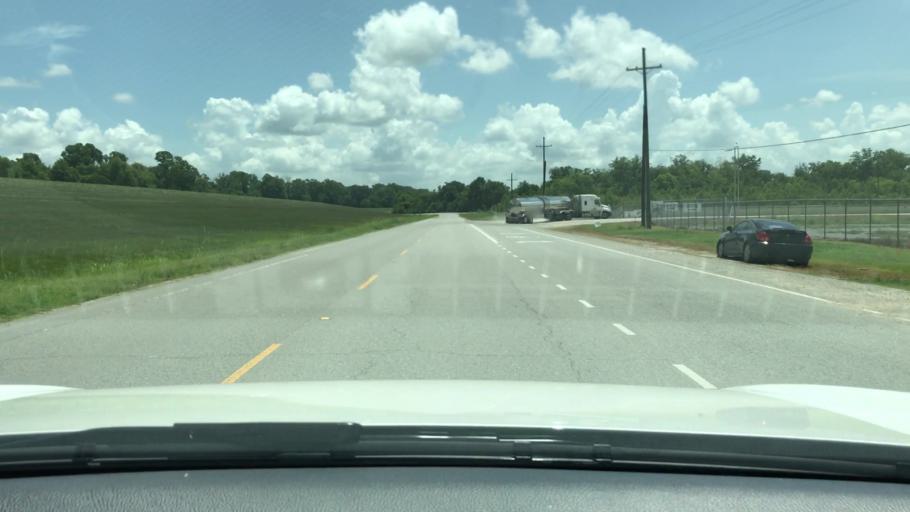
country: US
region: Louisiana
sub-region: Iberville Parish
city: Plaquemine
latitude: 30.2728
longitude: -91.1679
